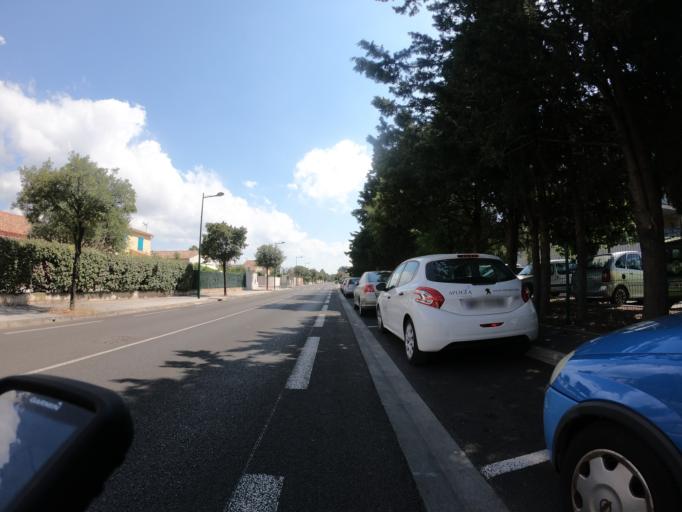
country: FR
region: Provence-Alpes-Cote d'Azur
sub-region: Departement du Var
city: La Garde
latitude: 43.1281
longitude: 6.0227
